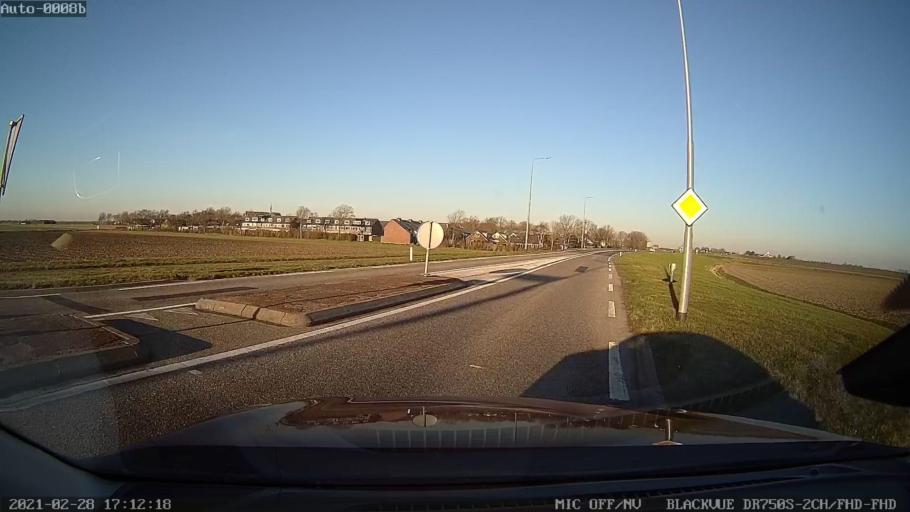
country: NL
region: Zeeland
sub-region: Schouwen-Duiveland
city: Scharendijke
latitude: 51.7194
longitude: 3.9068
